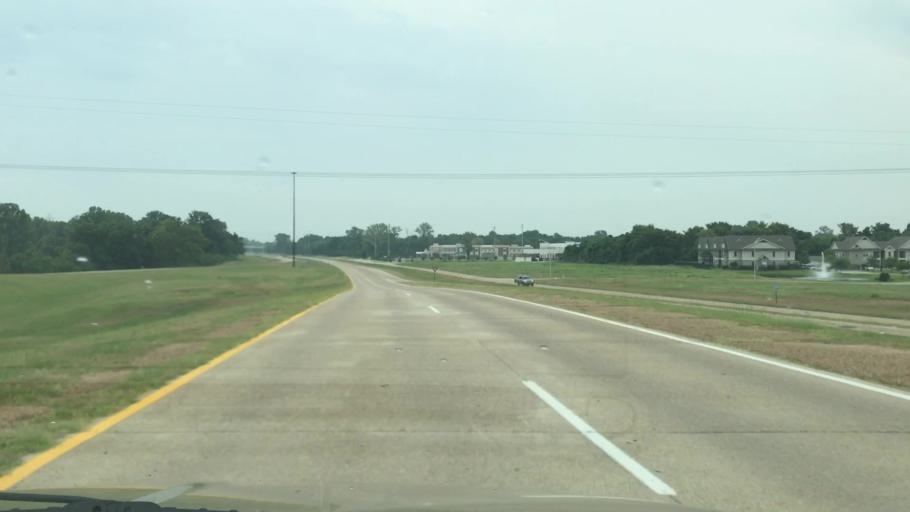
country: US
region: Louisiana
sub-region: Bossier Parish
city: Bossier City
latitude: 32.4999
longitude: -93.7154
